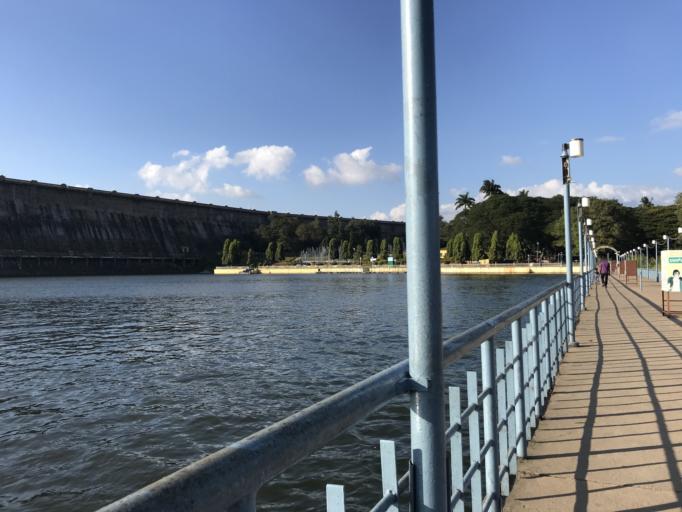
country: IN
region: Karnataka
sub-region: Mandya
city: Shrirangapattana
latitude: 12.4251
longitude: 76.5744
